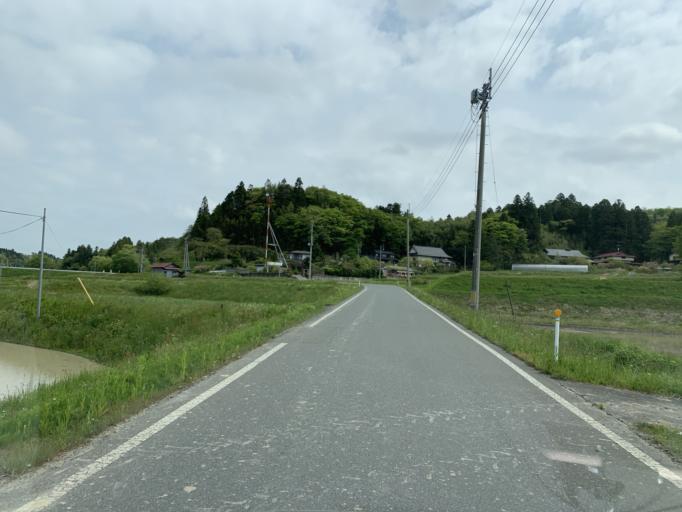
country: JP
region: Iwate
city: Ichinoseki
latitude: 38.8505
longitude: 141.1967
